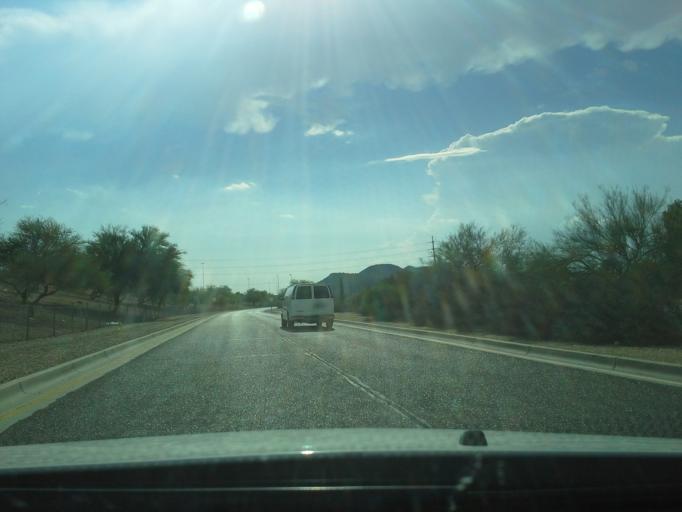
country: US
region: Arizona
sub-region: Maricopa County
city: Peoria
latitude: 33.6693
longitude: -112.1297
